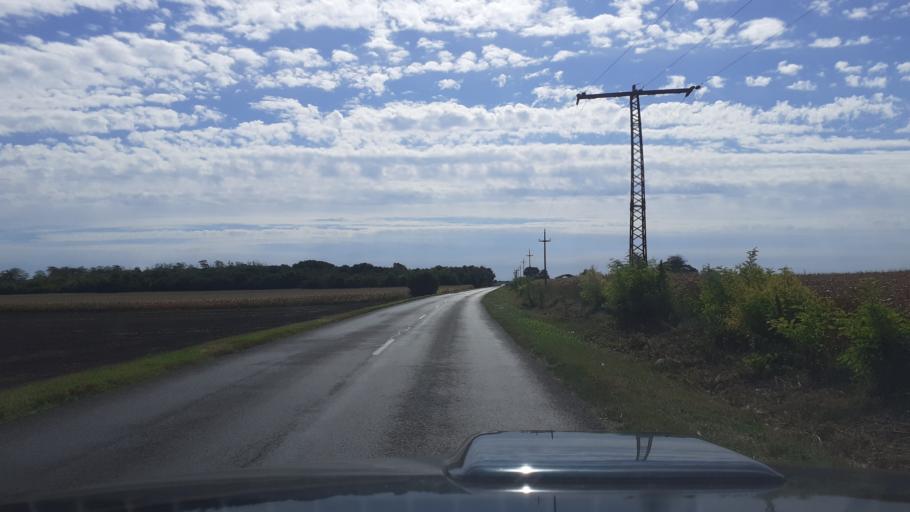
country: HU
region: Fejer
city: Pusztaszabolcs
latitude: 47.1232
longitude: 18.6877
